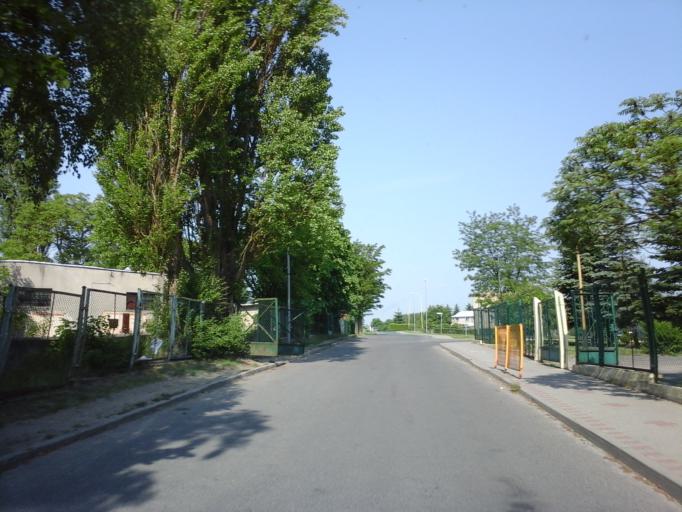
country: PL
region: West Pomeranian Voivodeship
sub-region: Powiat stargardzki
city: Dobrzany
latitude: 53.3561
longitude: 15.4217
